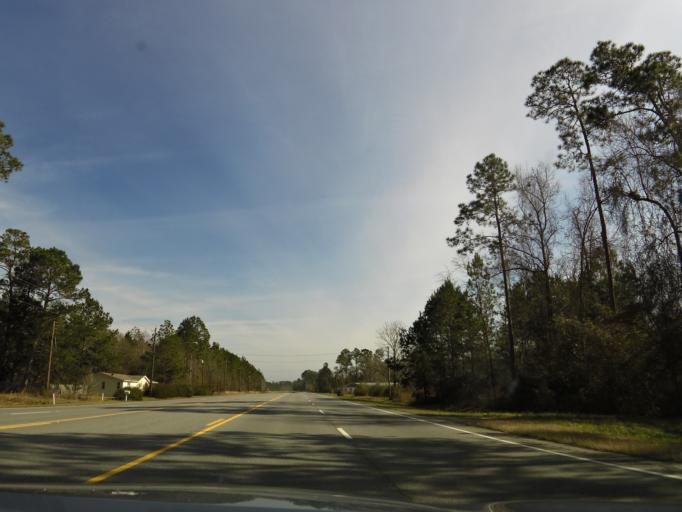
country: US
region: Georgia
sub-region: Lanier County
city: Lakeland
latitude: 30.9109
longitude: -83.0735
